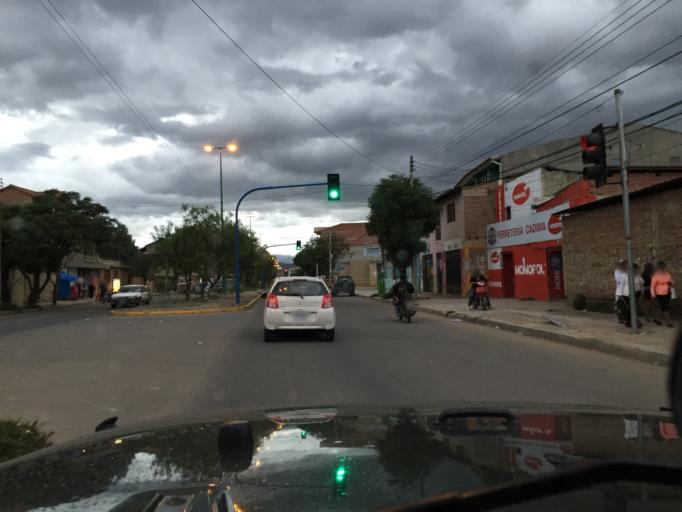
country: BO
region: Cochabamba
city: Cochabamba
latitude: -17.3970
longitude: -66.1945
